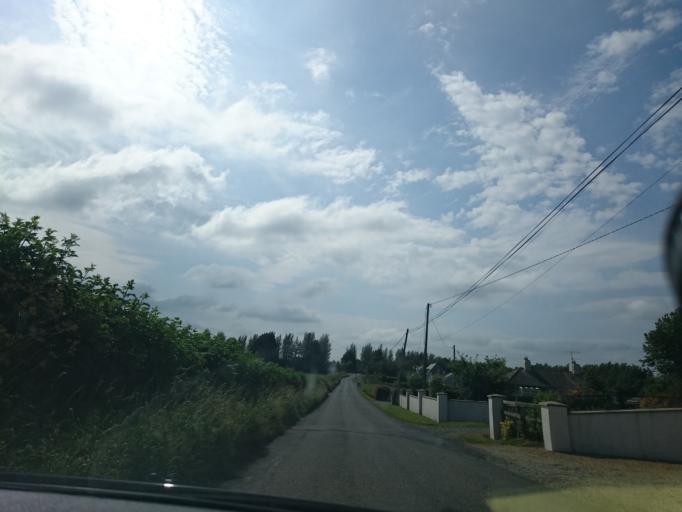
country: IE
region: Leinster
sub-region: Kilkenny
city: Thomastown
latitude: 52.5284
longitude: -7.2087
